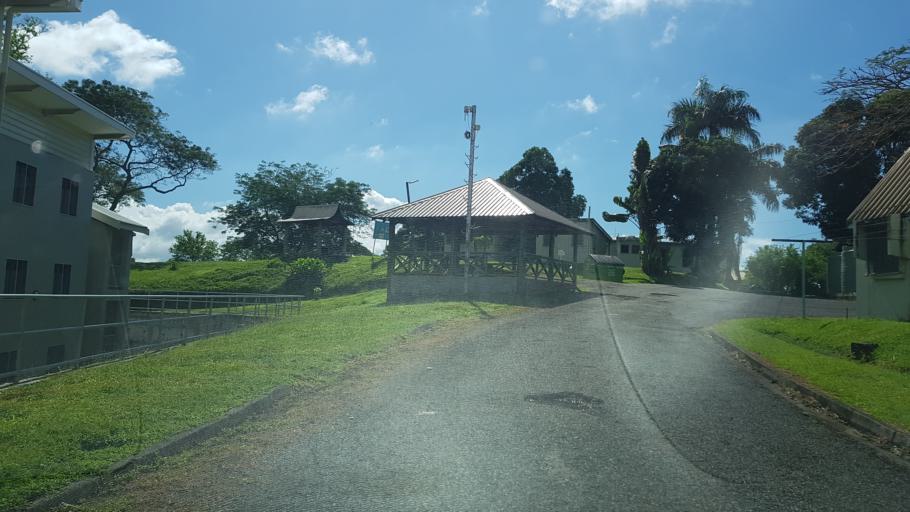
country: FJ
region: Central
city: Suva
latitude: -18.1496
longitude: 178.4411
